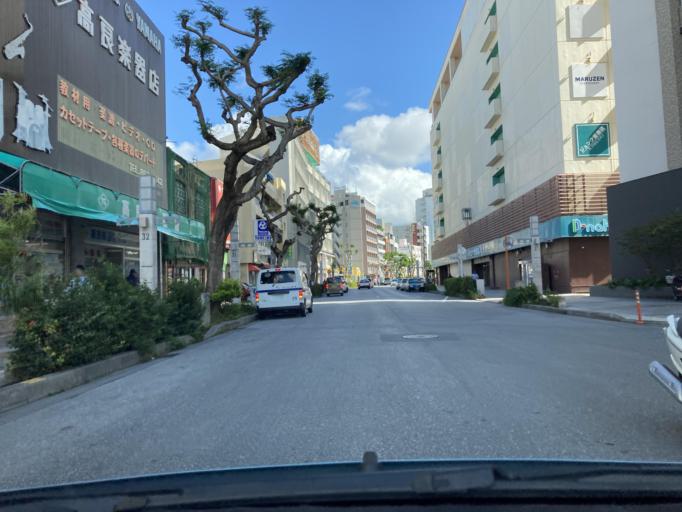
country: JP
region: Okinawa
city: Naha-shi
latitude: 26.2192
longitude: 127.6854
